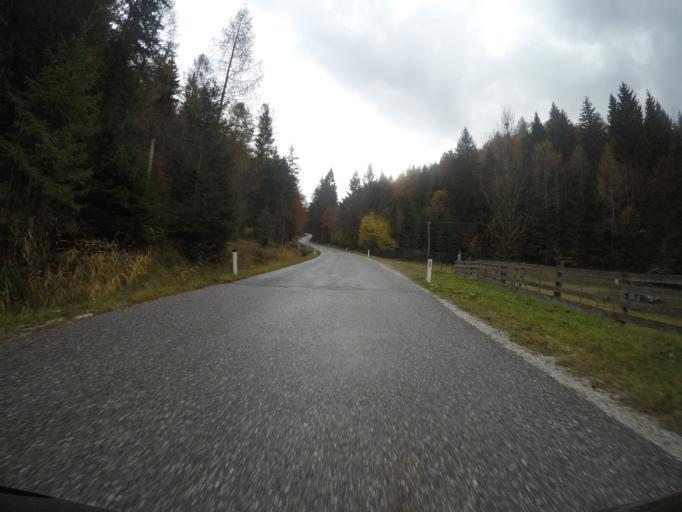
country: SI
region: Kranjska Gora
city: Mojstrana
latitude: 46.4474
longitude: 13.9327
